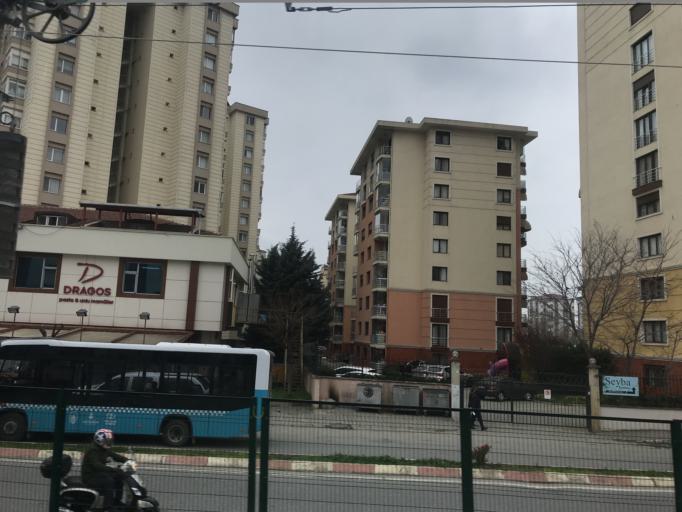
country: TR
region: Istanbul
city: Maltepe
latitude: 40.9009
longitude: 29.1667
